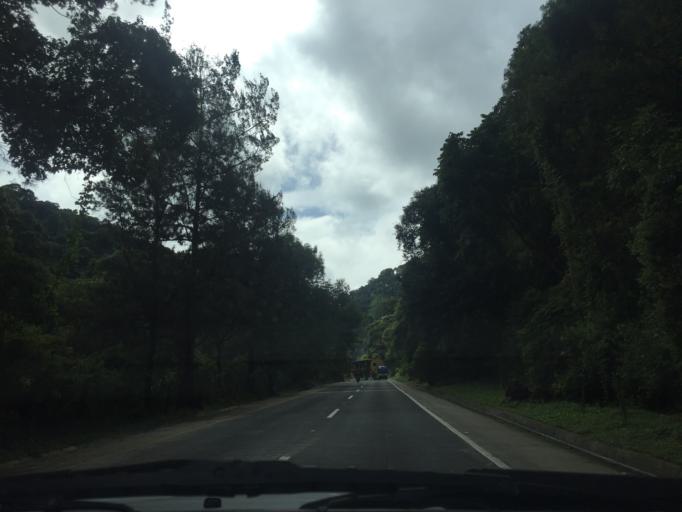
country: GT
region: Sacatepequez
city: Santa Lucia Milpas Altas
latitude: 14.5610
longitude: -90.6929
